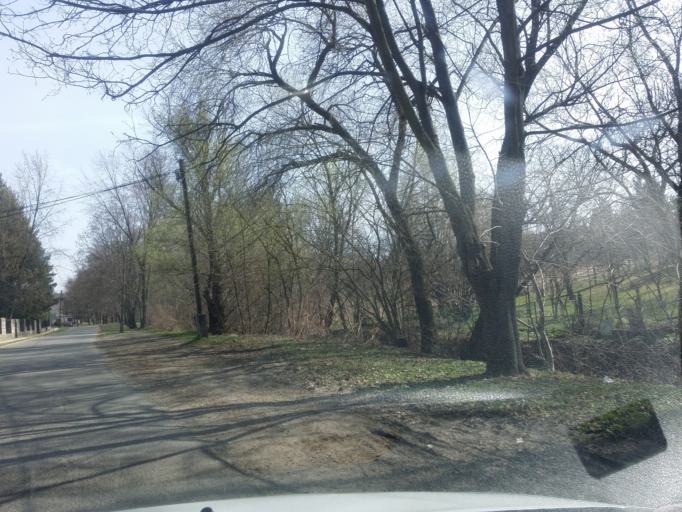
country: HU
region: Pest
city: Kismaros
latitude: 47.8665
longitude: 19.0036
